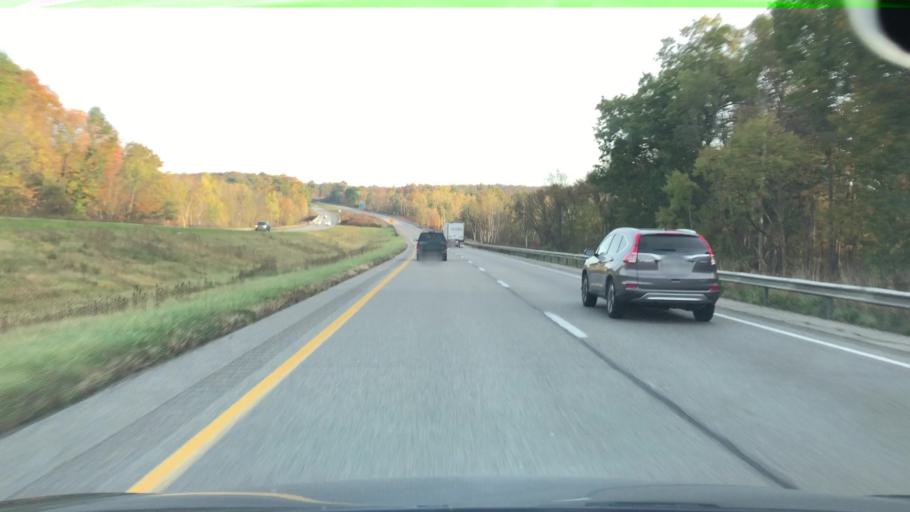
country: US
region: Pennsylvania
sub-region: Mercer County
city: Stoneboro
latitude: 41.3652
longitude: -80.1574
